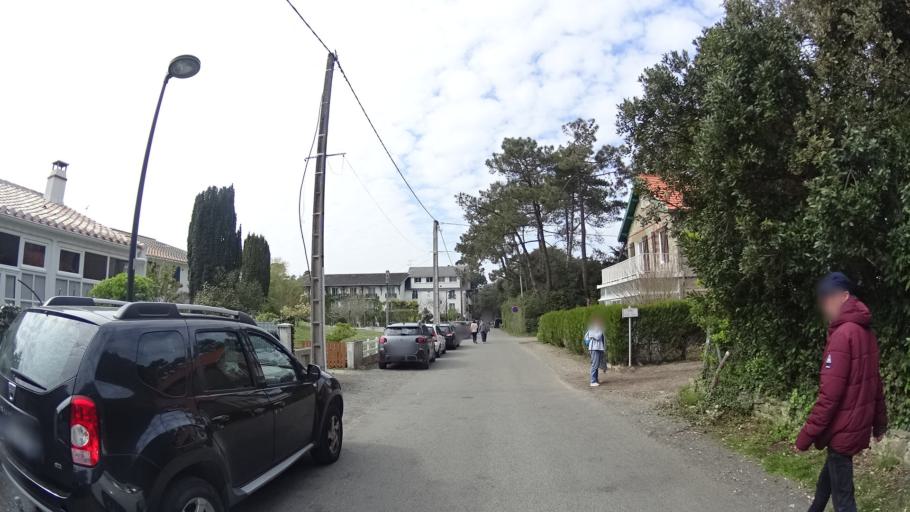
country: FR
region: Pays de la Loire
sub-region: Departement de la Vendee
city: La Gueriniere
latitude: 47.0104
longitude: -2.2257
